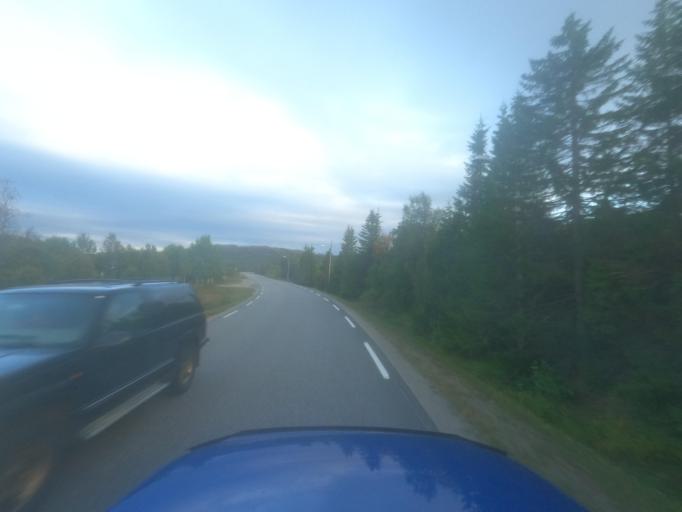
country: NO
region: Finnmark Fylke
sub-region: Porsanger
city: Lakselv
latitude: 70.3512
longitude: 25.0375
